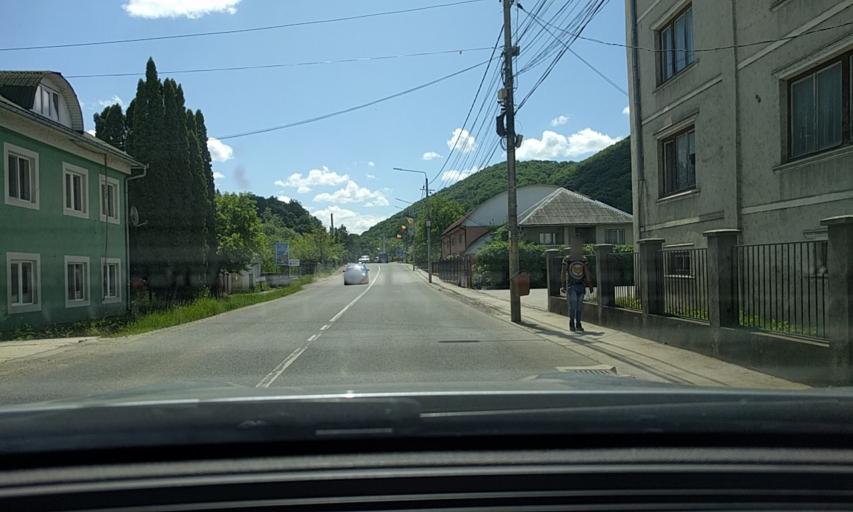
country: RO
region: Bistrita-Nasaud
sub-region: Oras Nasaud
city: Nasaud
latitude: 47.2812
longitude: 24.4204
